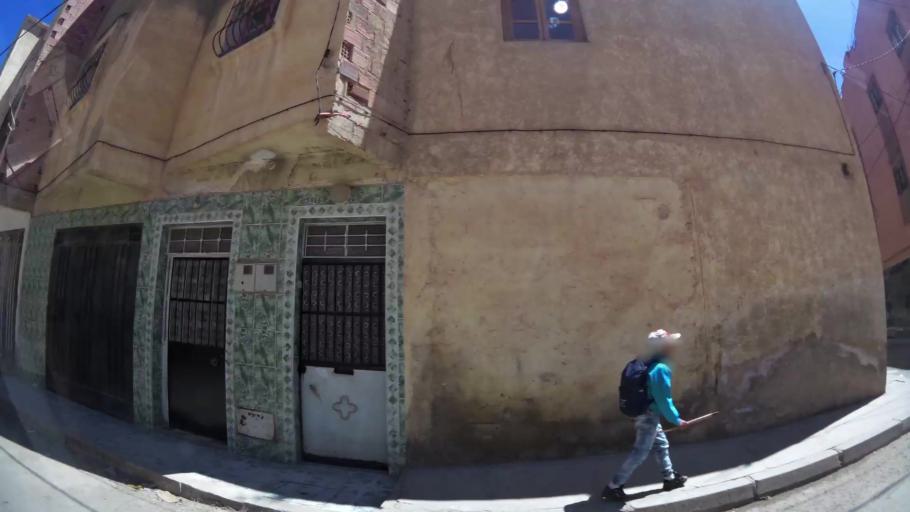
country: MA
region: Oriental
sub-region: Oujda-Angad
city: Oujda
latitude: 34.6600
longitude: -1.8830
